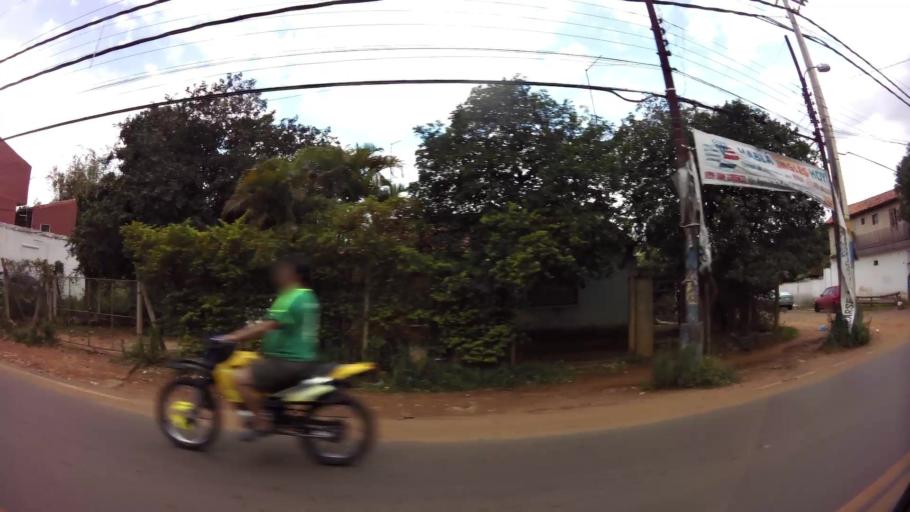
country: PY
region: Central
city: San Lorenzo
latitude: -25.2835
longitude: -57.4832
